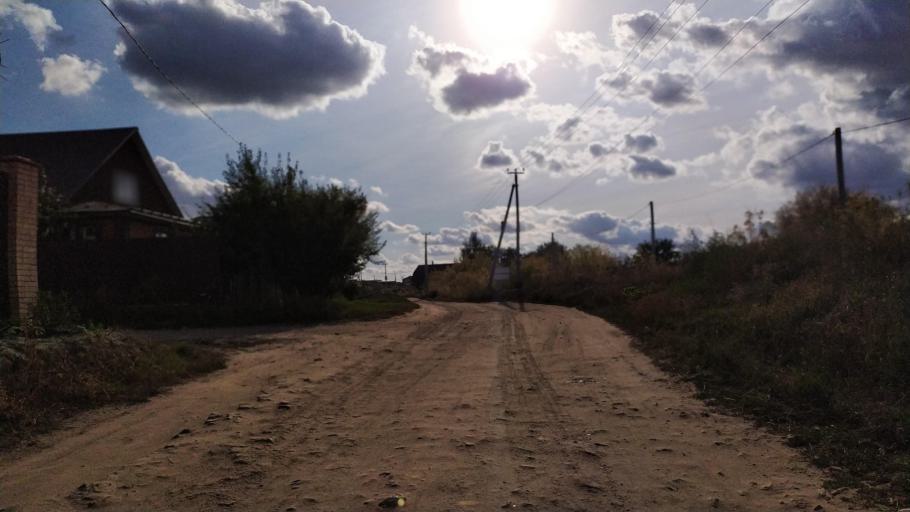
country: RU
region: Kursk
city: Kursk
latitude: 51.6395
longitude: 36.1526
